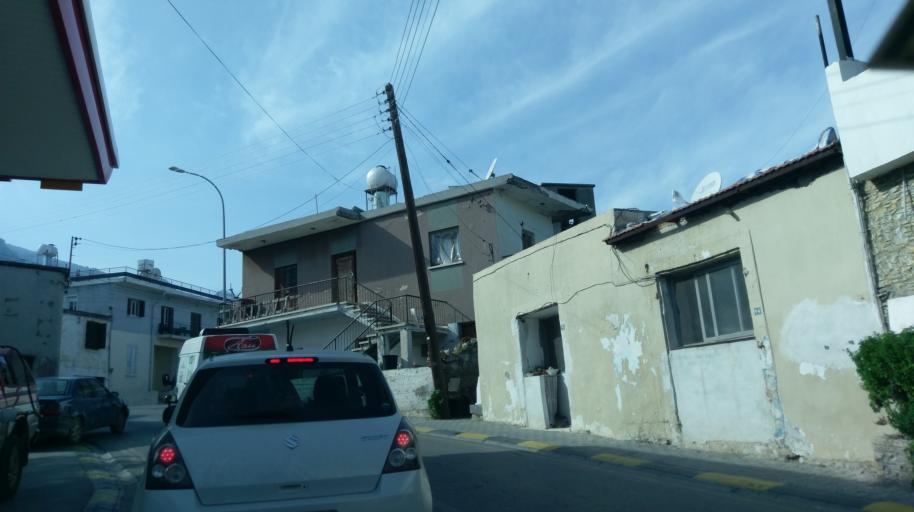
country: CY
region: Keryneia
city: Lapithos
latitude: 35.3404
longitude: 33.1815
